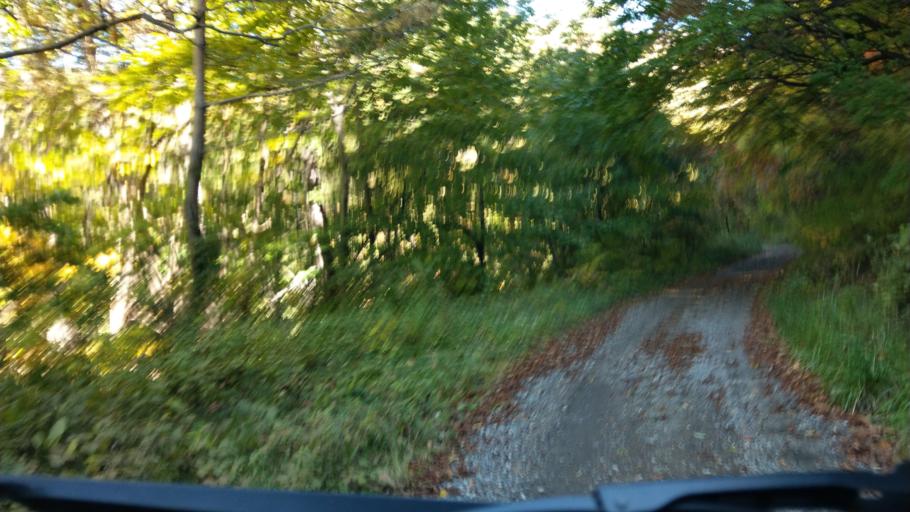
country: JP
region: Nagano
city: Komoro
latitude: 36.3759
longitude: 138.4300
